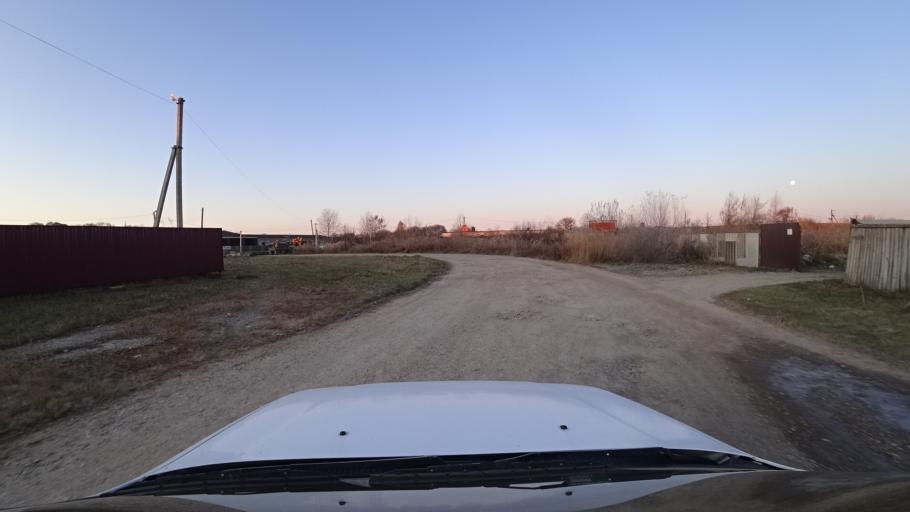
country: RU
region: Primorskiy
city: Dal'nerechensk
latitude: 45.9181
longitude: 133.7353
